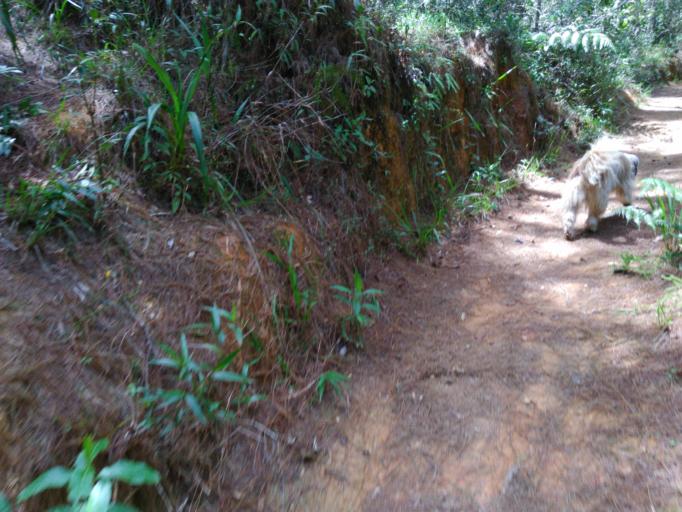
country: CO
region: Antioquia
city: Guarne
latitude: 6.2569
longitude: -75.4987
